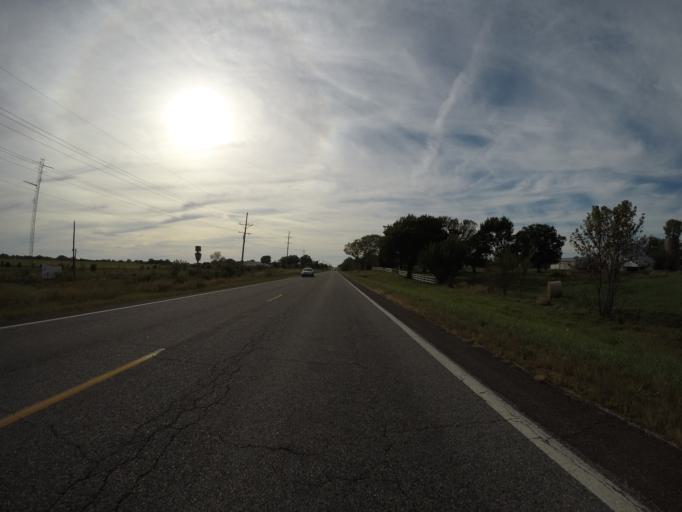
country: US
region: Kansas
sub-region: Franklin County
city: Wellsville
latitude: 38.7679
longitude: -95.0976
